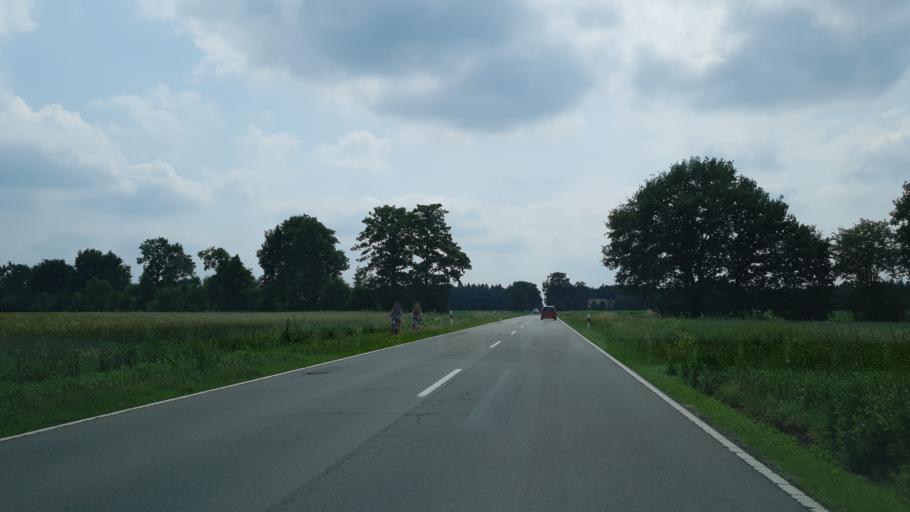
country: DE
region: Lower Saxony
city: Geeste
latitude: 52.5777
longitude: 7.2180
